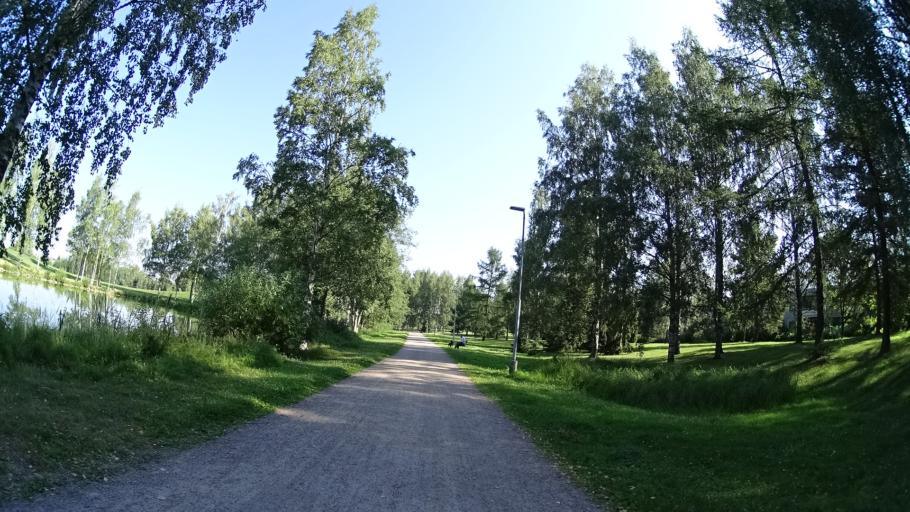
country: FI
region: Uusimaa
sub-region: Helsinki
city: Vantaa
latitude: 60.2766
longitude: 24.9853
